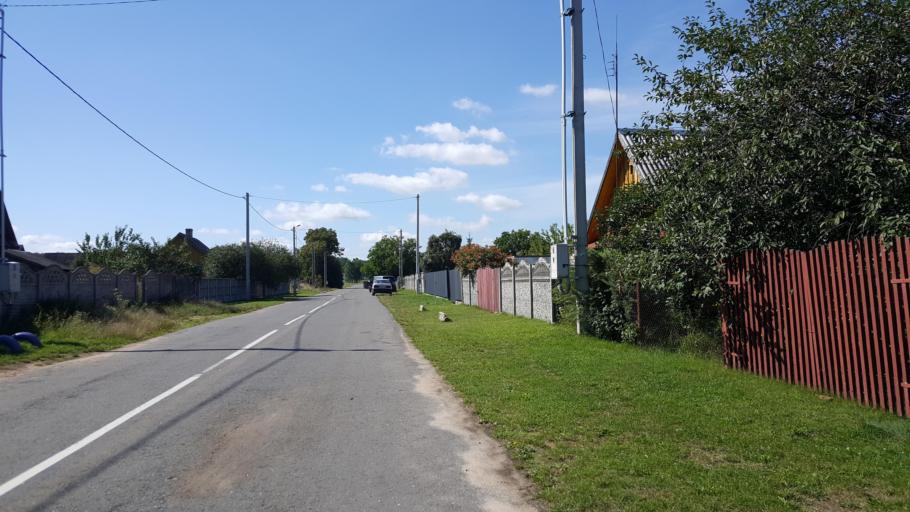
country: BY
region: Brest
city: Charnawchytsy
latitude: 52.3022
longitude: 23.7789
